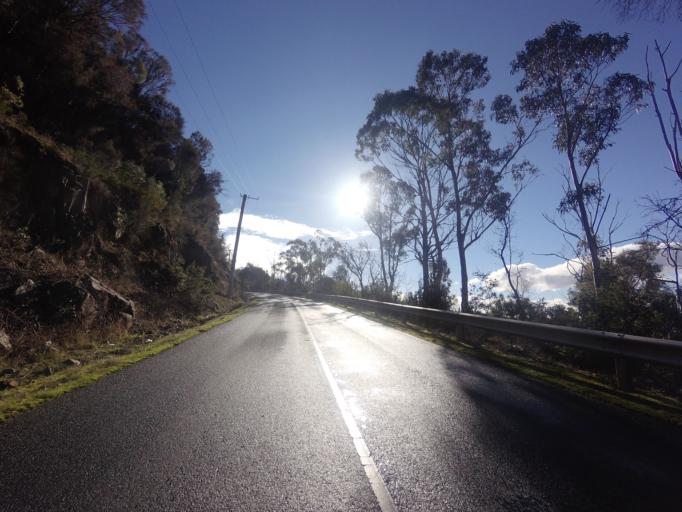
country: AU
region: Tasmania
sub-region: Glenorchy
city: Berriedale
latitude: -42.8244
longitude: 147.2074
